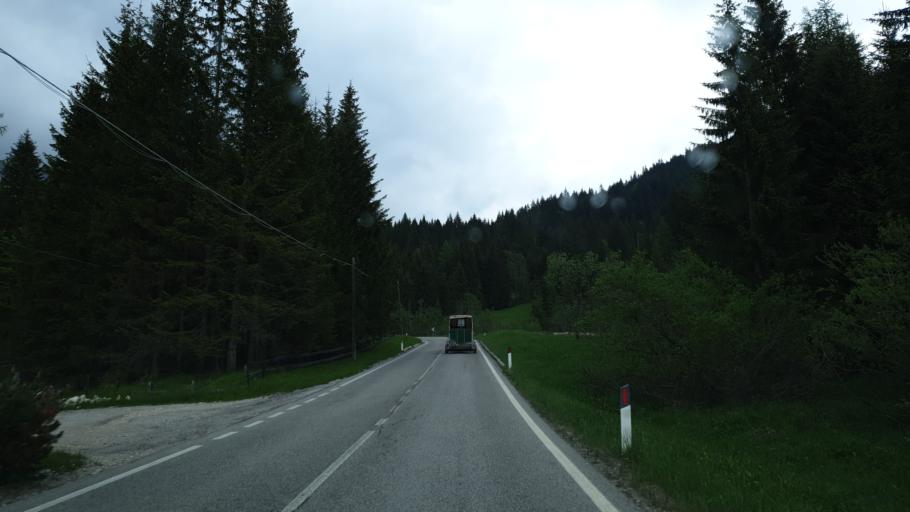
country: IT
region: Veneto
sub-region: Provincia di Belluno
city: San Vito
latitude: 46.5496
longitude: 12.2478
